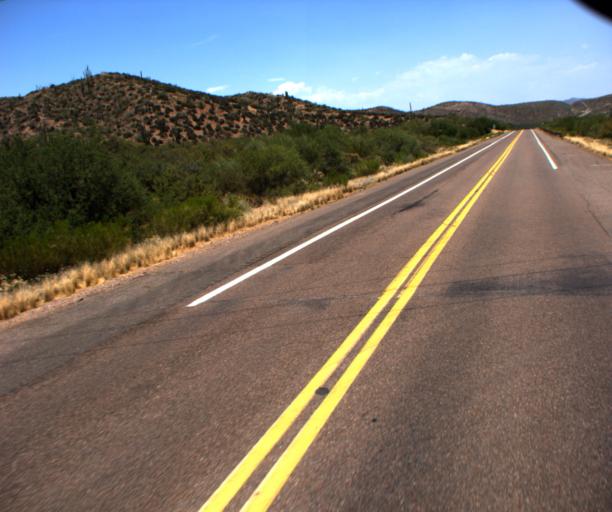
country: US
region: Arizona
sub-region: Gila County
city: Tonto Basin
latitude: 33.9643
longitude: -111.3247
